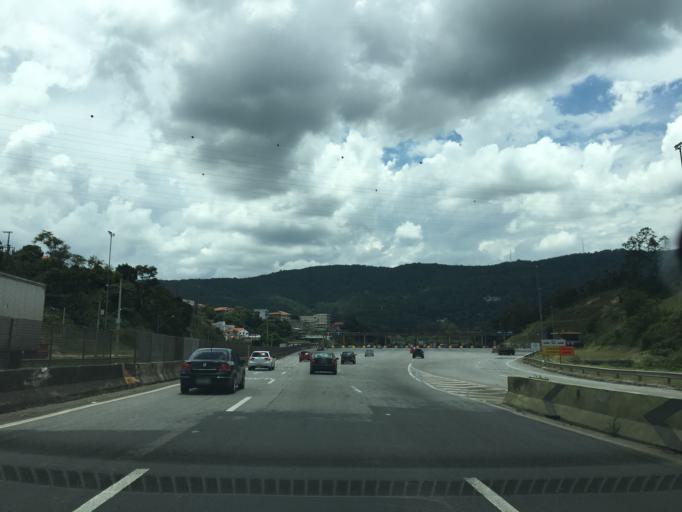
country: BR
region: Sao Paulo
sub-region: Mairipora
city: Mairipora
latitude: -23.3247
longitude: -46.5798
